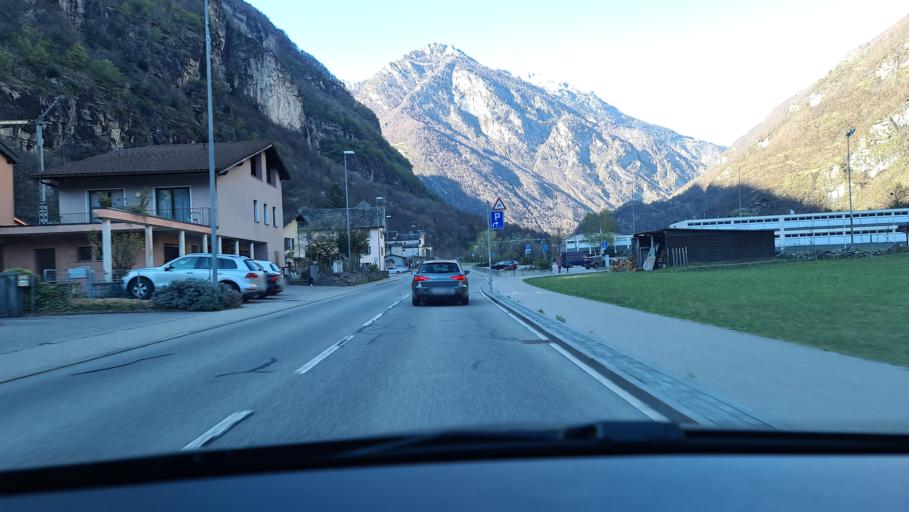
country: CH
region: Ticino
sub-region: Vallemaggia District
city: Cevio
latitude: 46.3192
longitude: 8.6023
